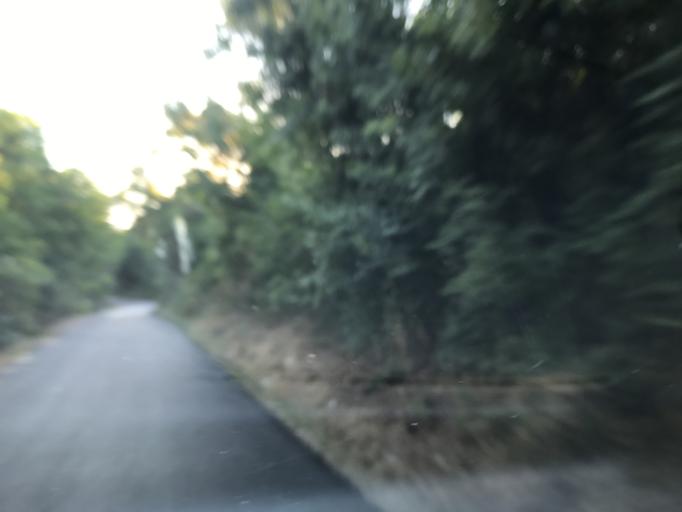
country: BG
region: Vidin
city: Bregovo
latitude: 44.1206
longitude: 22.5866
